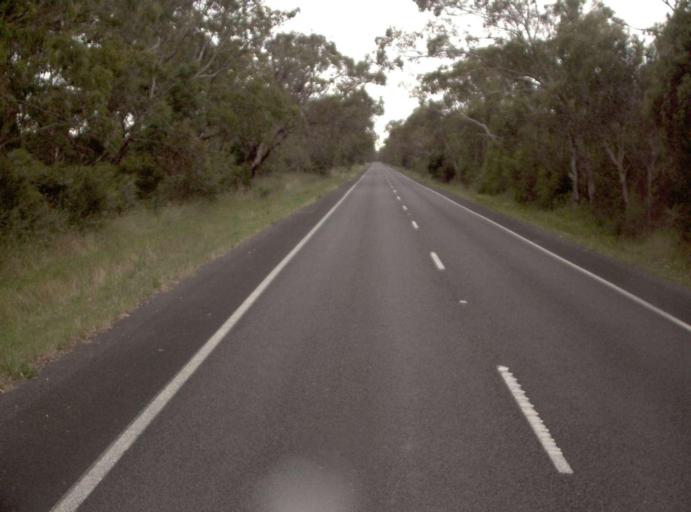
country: AU
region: Victoria
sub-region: Latrobe
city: Traralgon
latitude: -38.5515
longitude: 146.8208
